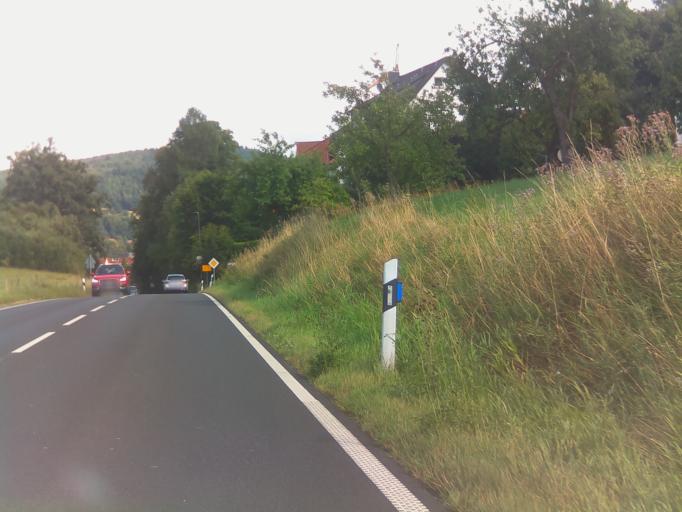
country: DE
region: Hesse
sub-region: Regierungsbezirk Darmstadt
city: Bad Orb
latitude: 50.2316
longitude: 9.3357
